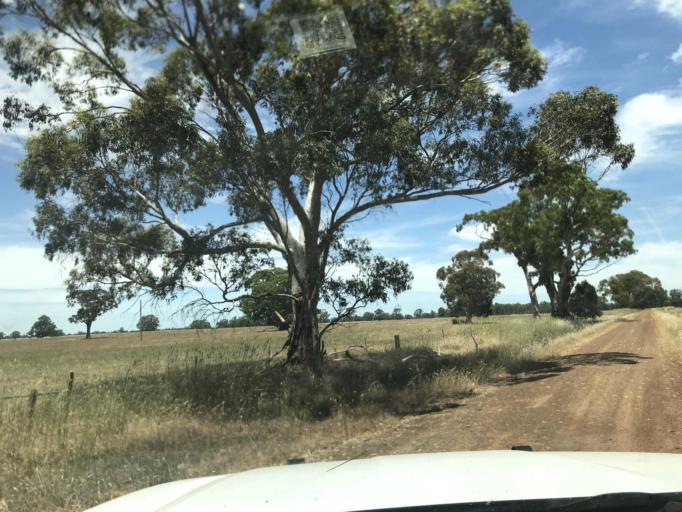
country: AU
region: Victoria
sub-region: Horsham
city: Horsham
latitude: -36.9865
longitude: 141.5109
